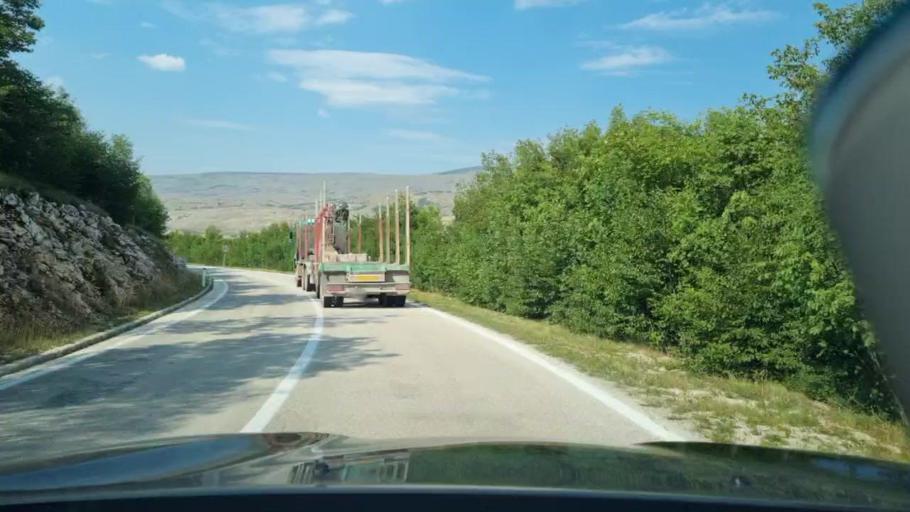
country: BA
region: Federation of Bosnia and Herzegovina
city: Glamoc
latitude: 43.9780
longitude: 16.9138
